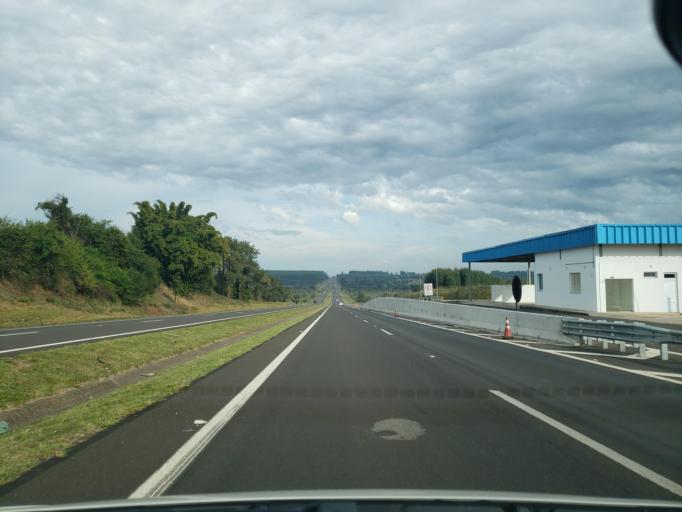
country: BR
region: Sao Paulo
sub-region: Itirapina
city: Itirapina
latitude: -22.2566
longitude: -47.8548
